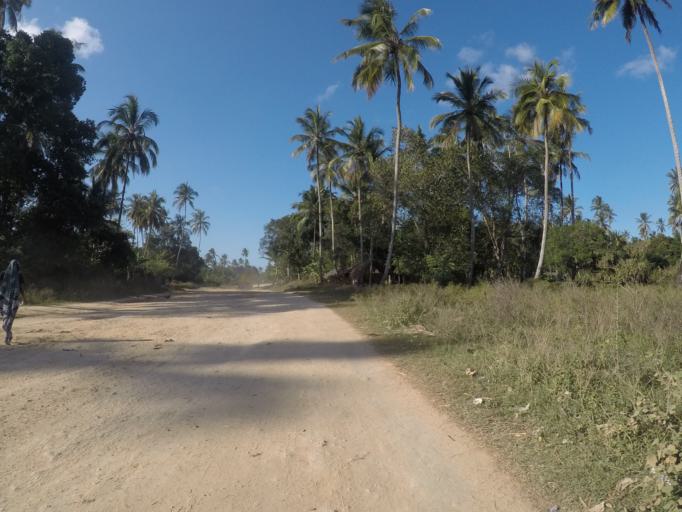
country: TZ
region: Zanzibar Central/South
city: Koani
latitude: -6.1752
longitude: 39.2840
